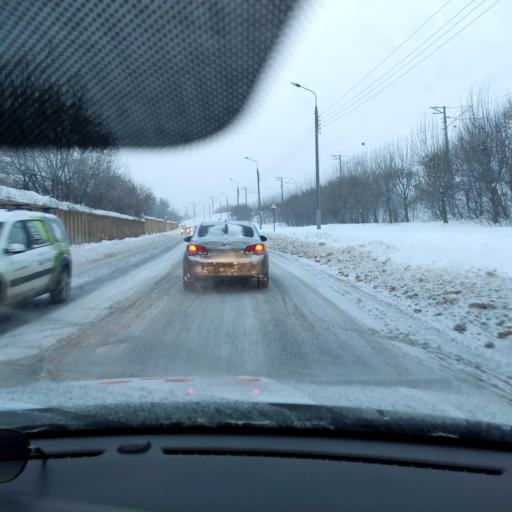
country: RU
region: Tatarstan
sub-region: Gorod Kazan'
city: Kazan
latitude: 55.7285
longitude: 49.1815
